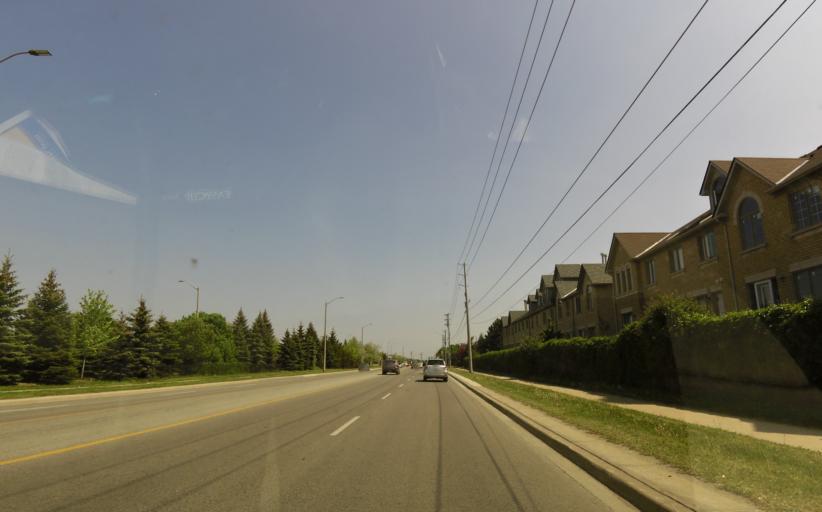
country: CA
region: Ontario
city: Mississauga
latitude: 43.6199
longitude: -79.6471
